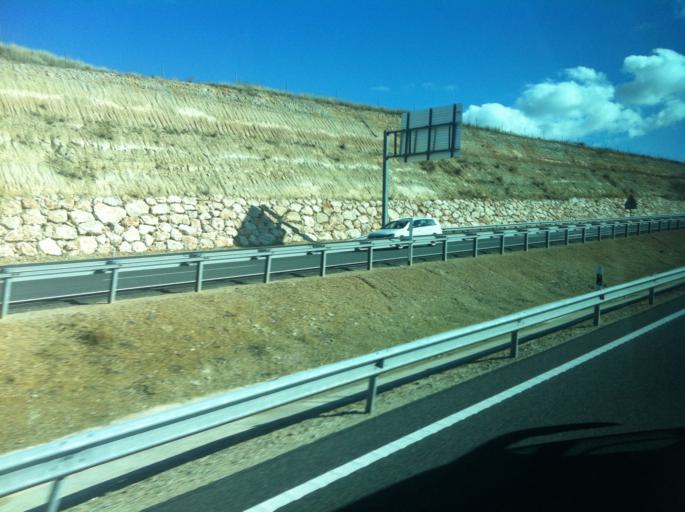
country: ES
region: Castille and Leon
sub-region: Provincia de Burgos
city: Bahabon de Esgueva
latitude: 41.8901
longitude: -3.7408
